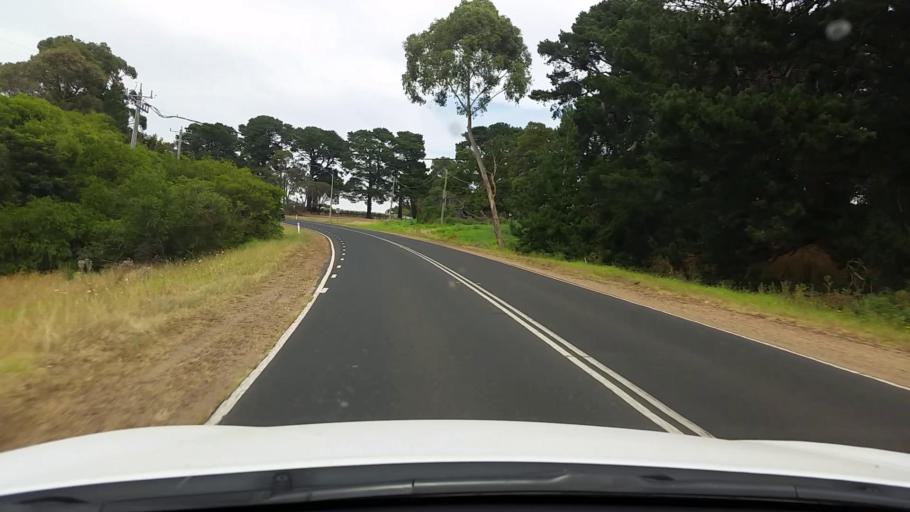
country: AU
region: Victoria
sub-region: Mornington Peninsula
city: Merricks
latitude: -38.4185
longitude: 145.0452
